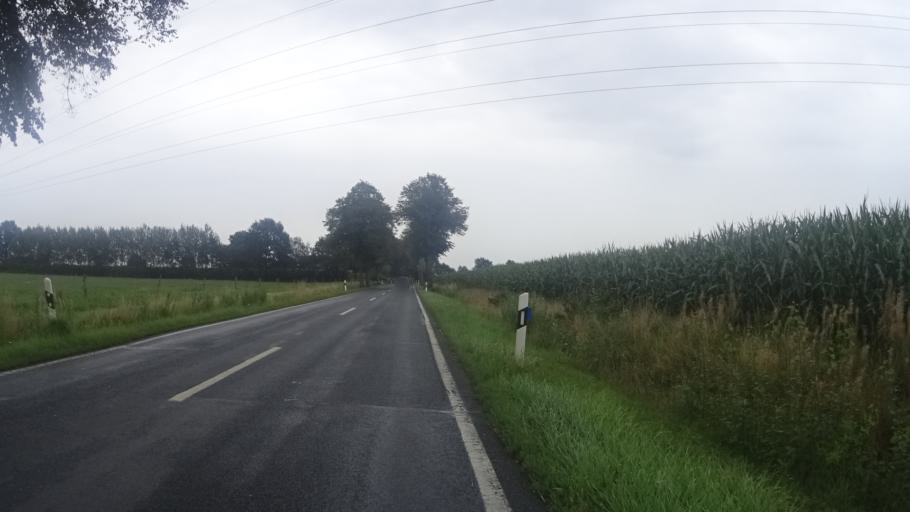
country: DE
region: Schleswig-Holstein
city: Bullenkuhlen
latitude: 53.7564
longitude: 9.7424
